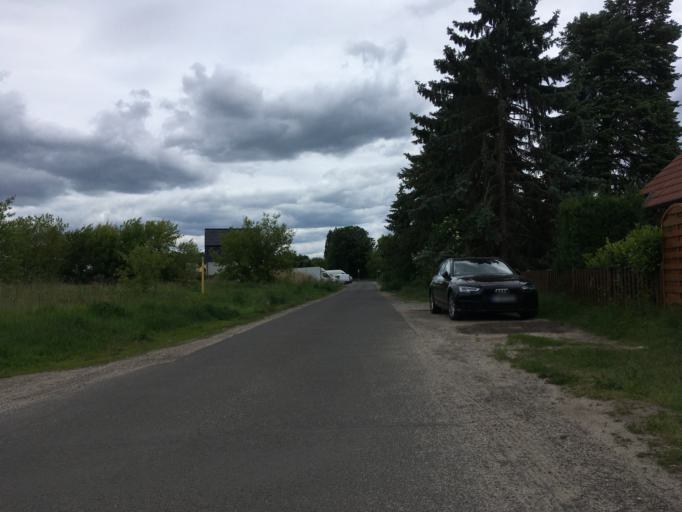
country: DE
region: Berlin
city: Biesdorf
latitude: 52.5081
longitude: 13.5451
